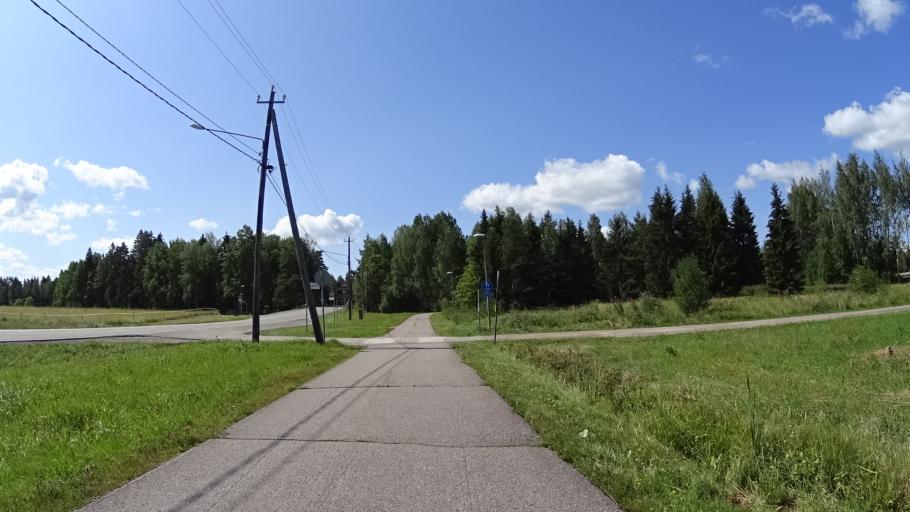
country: FI
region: Uusimaa
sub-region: Helsinki
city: Jaervenpaeae
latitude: 60.4622
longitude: 25.0600
